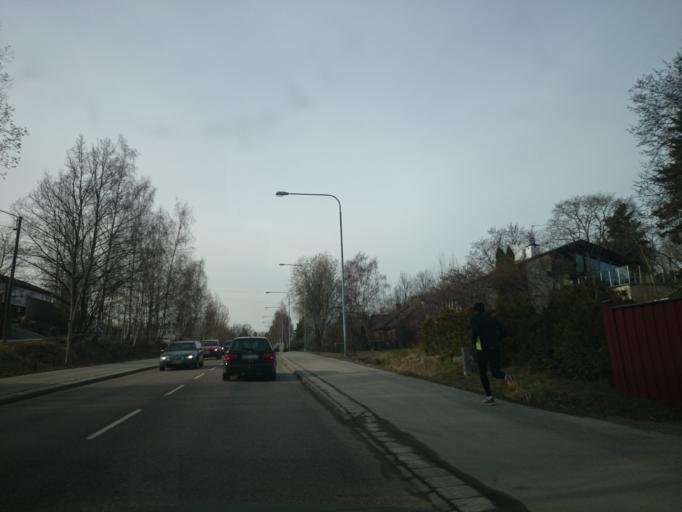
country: SE
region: Stockholm
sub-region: Huddinge Kommun
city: Huddinge
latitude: 59.2624
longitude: 17.9716
